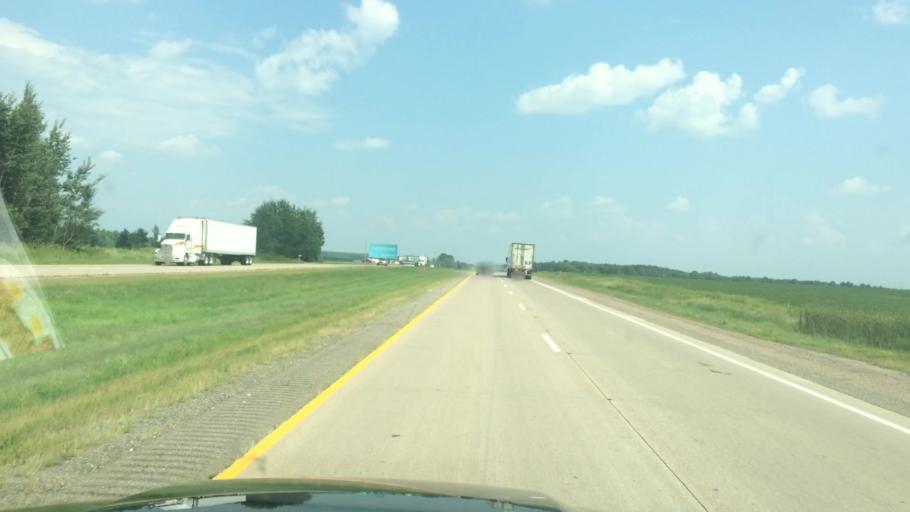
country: US
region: Wisconsin
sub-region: Marathon County
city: Athens
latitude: 44.9455
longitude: -90.1305
